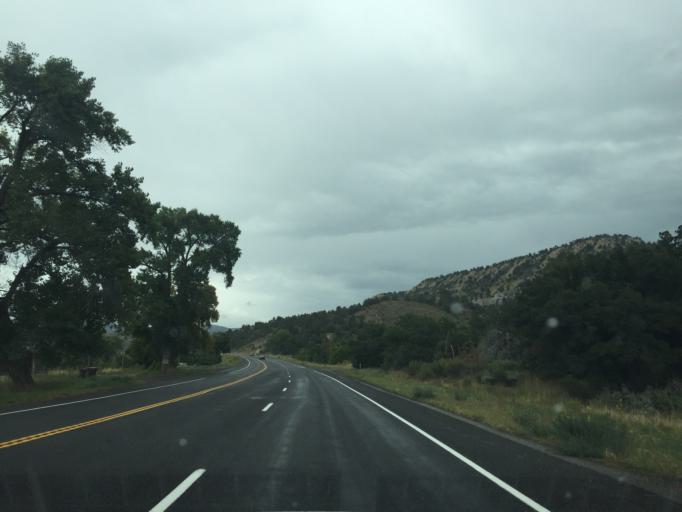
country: US
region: Utah
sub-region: Kane County
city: Kanab
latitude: 37.3038
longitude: -112.6018
